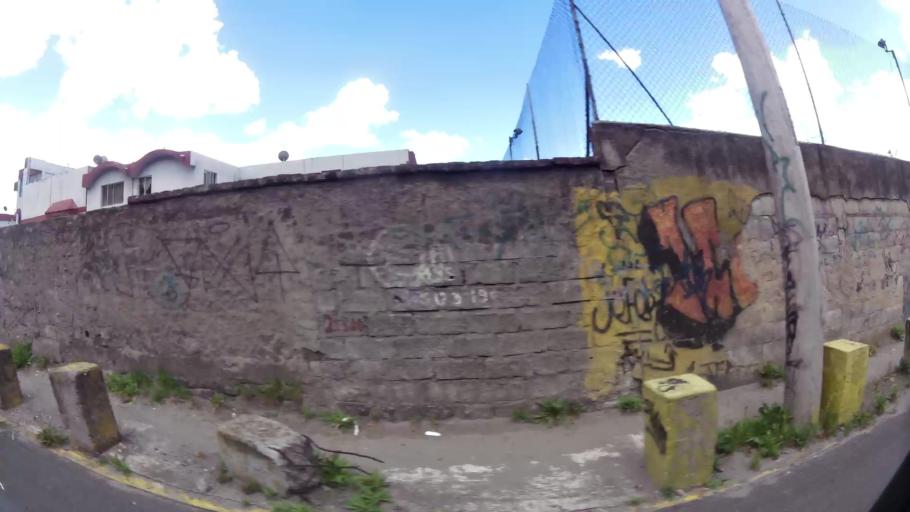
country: EC
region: Pichincha
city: Quito
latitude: -0.1865
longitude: -78.5107
